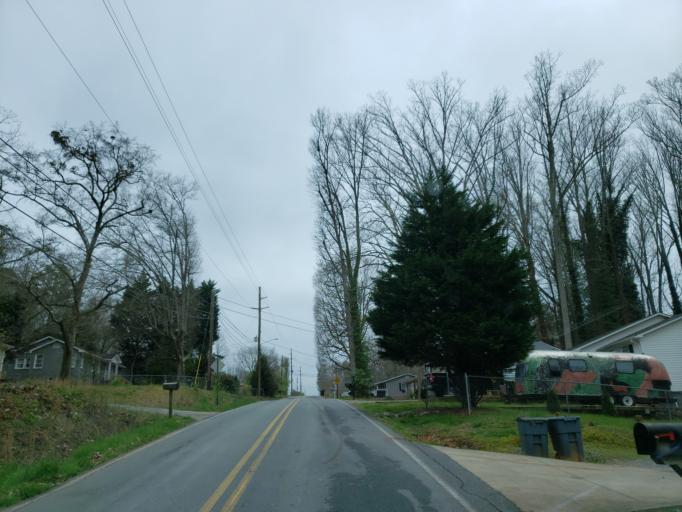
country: US
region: Georgia
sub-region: Pickens County
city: Jasper
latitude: 34.4645
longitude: -84.4220
